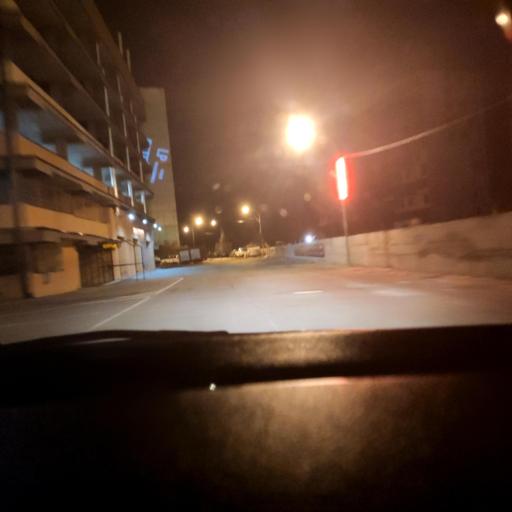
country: RU
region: Voronezj
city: Voronezh
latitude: 51.7153
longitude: 39.1907
